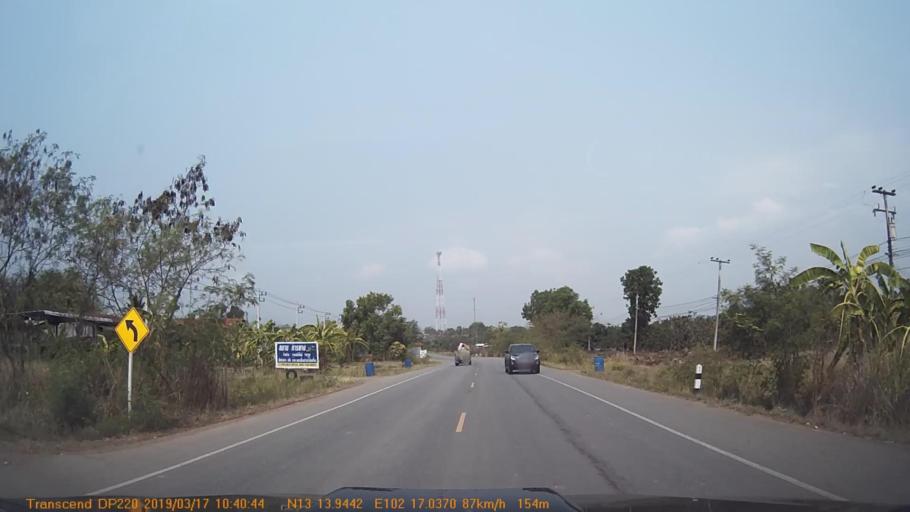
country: TH
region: Chanthaburi
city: Soi Dao
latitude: 13.2325
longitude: 102.2837
